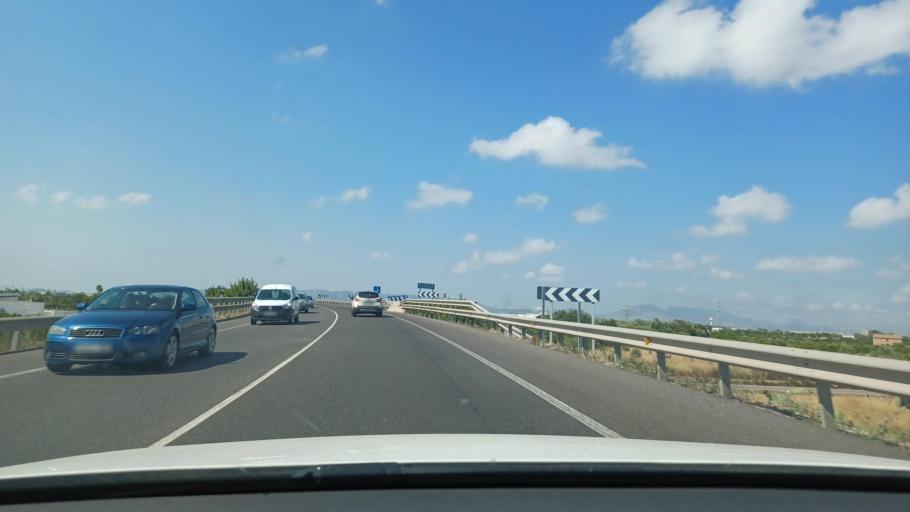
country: ES
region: Valencia
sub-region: Provincia de Castello
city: Vila-real
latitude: 39.9403
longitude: -0.0861
